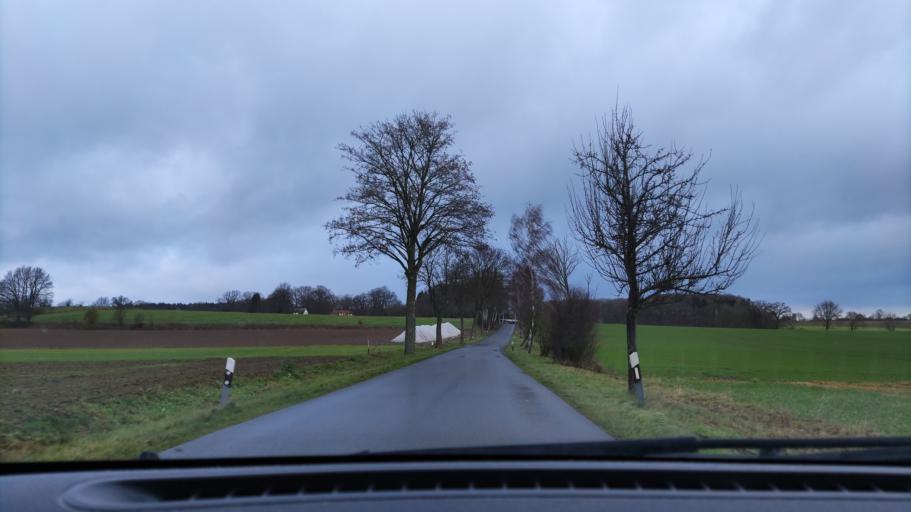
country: DE
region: Lower Saxony
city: Natendorf
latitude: 53.0900
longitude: 10.4428
